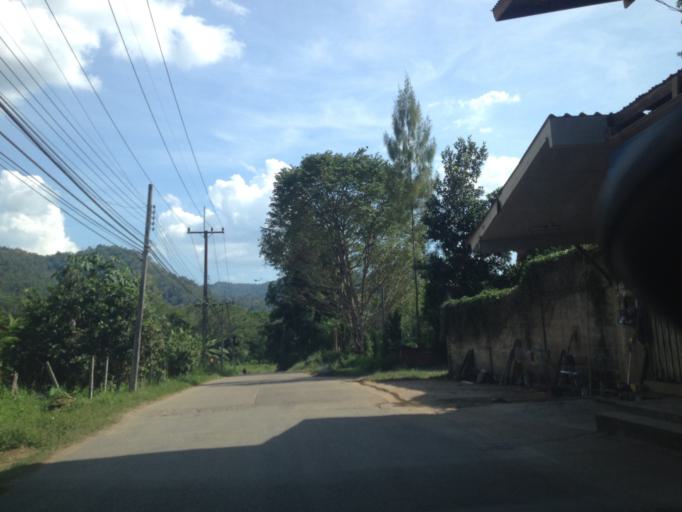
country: TH
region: Chiang Mai
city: Samoeng
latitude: 18.8625
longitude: 98.7252
